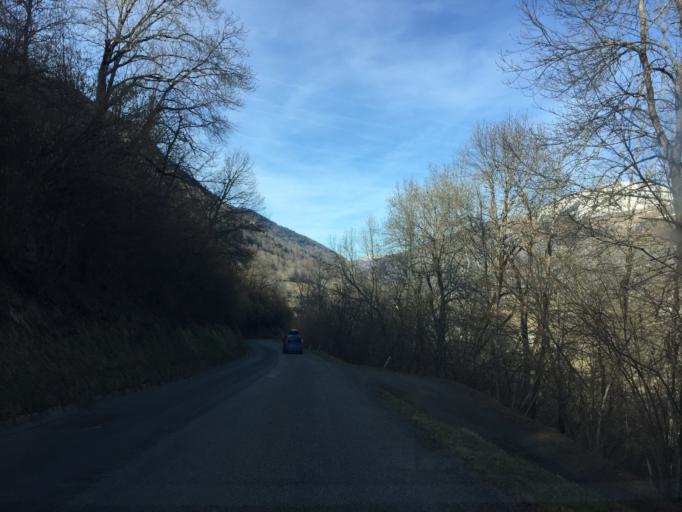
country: FR
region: Midi-Pyrenees
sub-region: Departement des Hautes-Pyrenees
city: Saint-Lary-Soulan
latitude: 42.8022
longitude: 0.4011
